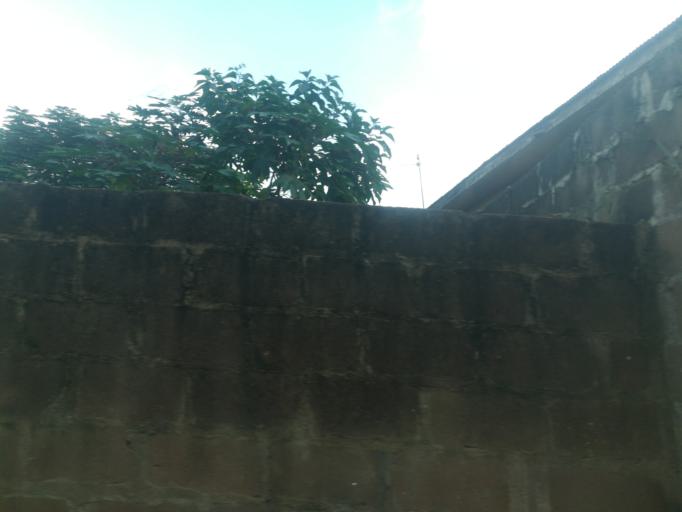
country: NG
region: Oyo
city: Ibadan
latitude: 7.3529
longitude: 3.8737
